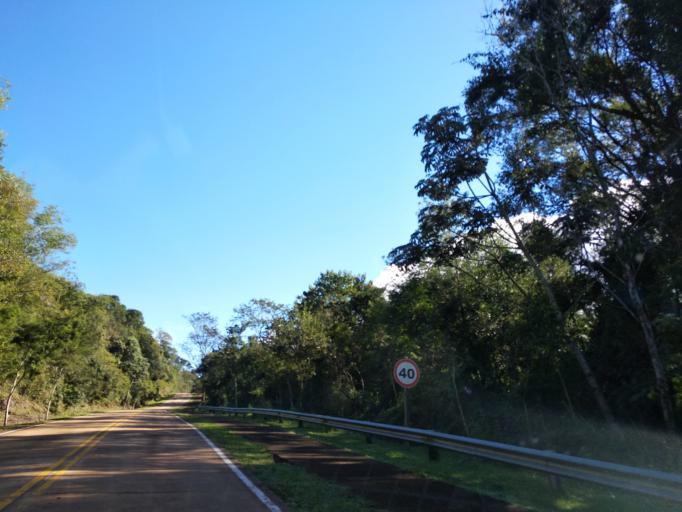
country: AR
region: Misiones
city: Cerro Cora
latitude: -27.4530
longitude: -55.5728
